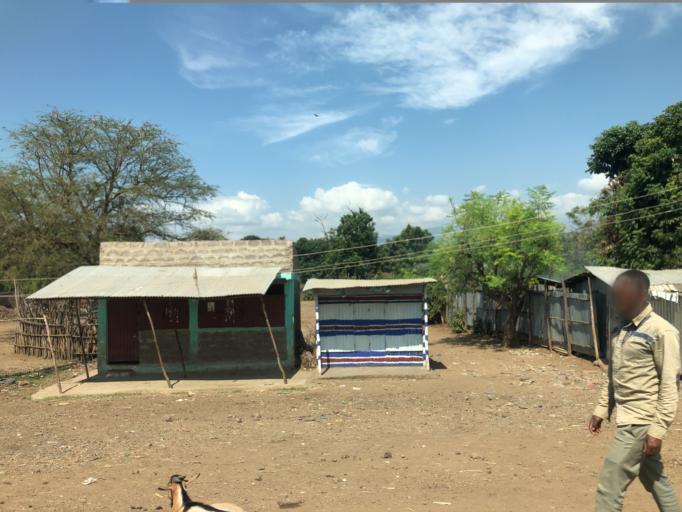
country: ET
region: Southern Nations, Nationalities, and People's Region
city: Arba Minch'
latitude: 5.8428
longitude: 37.4633
